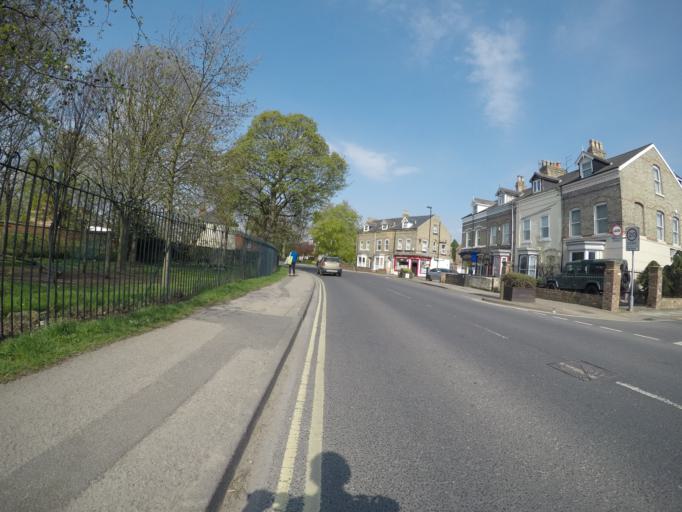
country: GB
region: England
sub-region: City of York
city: York
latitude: 53.9698
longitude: -1.0786
